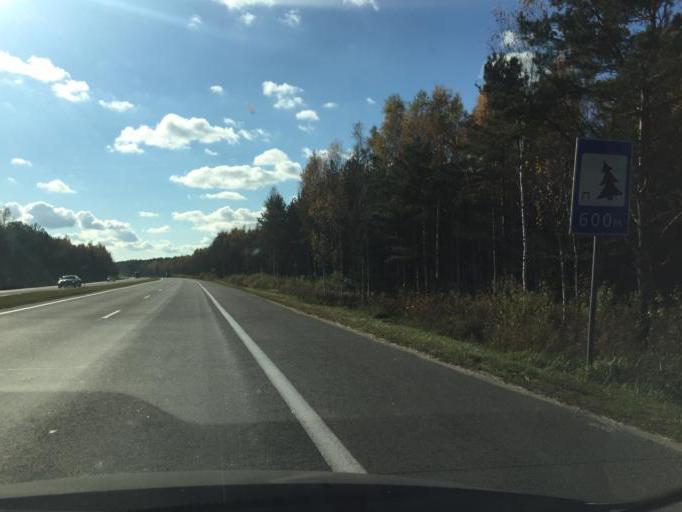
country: BY
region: Minsk
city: Slabada
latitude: 53.9391
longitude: 27.9649
